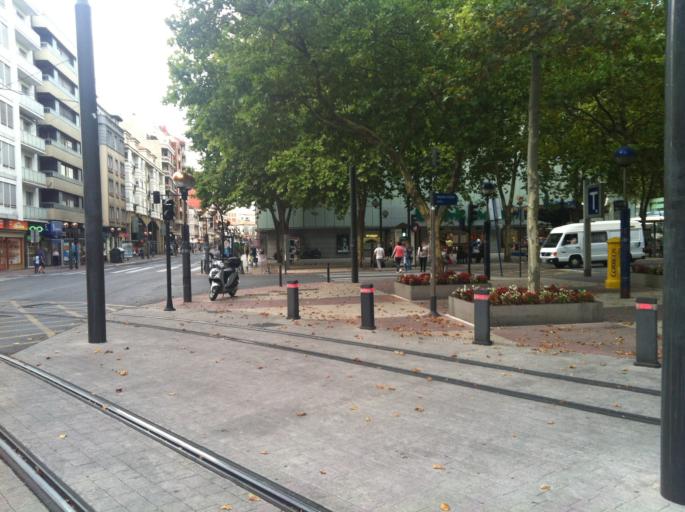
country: ES
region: Basque Country
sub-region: Provincia de Alava
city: Gasteiz / Vitoria
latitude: 42.8438
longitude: -2.6682
